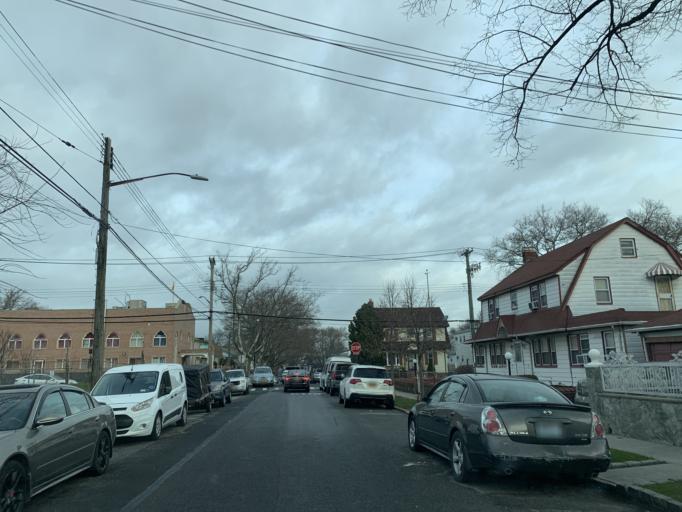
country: US
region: New York
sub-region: Queens County
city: Jamaica
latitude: 40.6860
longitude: -73.8098
